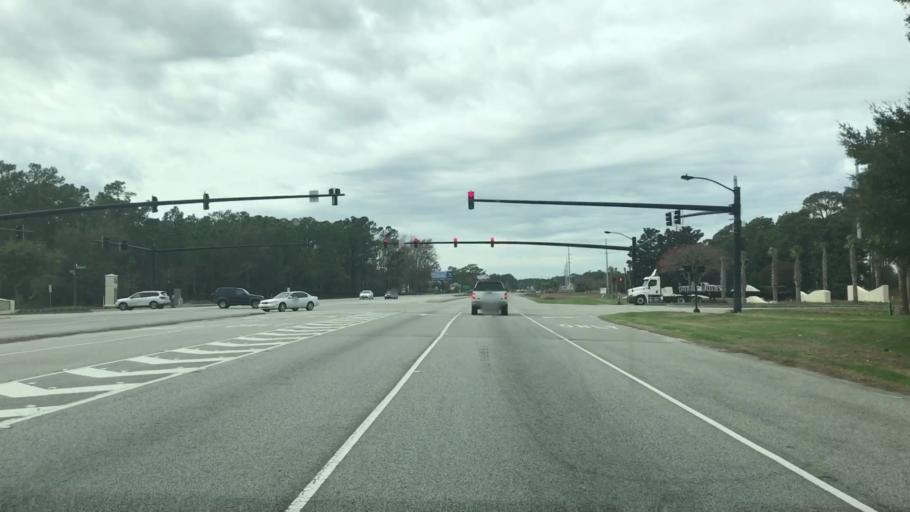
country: US
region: South Carolina
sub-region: Horry County
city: Myrtle Beach
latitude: 33.7645
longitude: -78.8111
